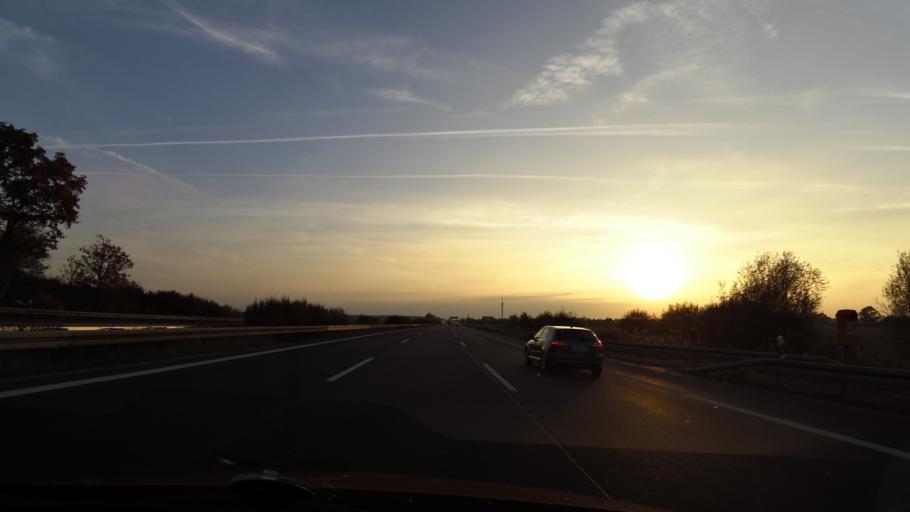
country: DE
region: Saxony-Anhalt
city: Vockerode
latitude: 51.8318
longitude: 12.3185
